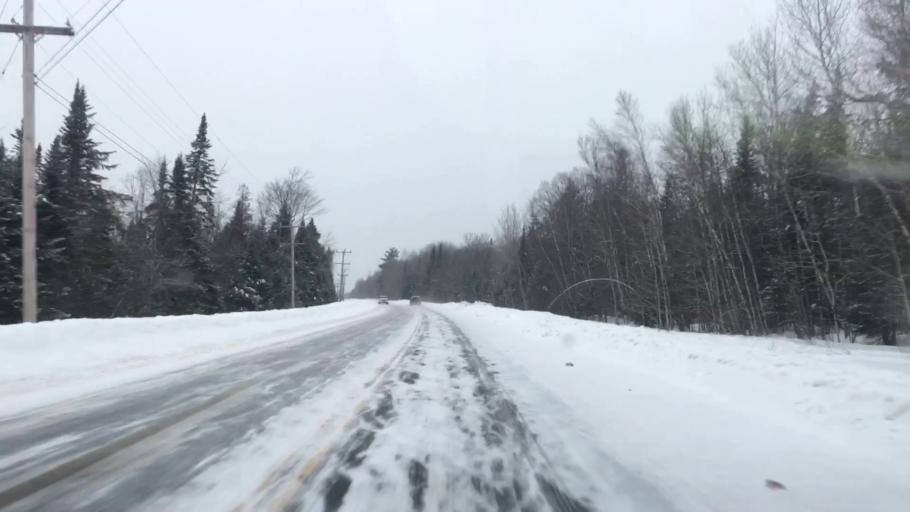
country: US
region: Maine
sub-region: Penobscot County
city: Medway
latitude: 45.5842
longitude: -68.4279
